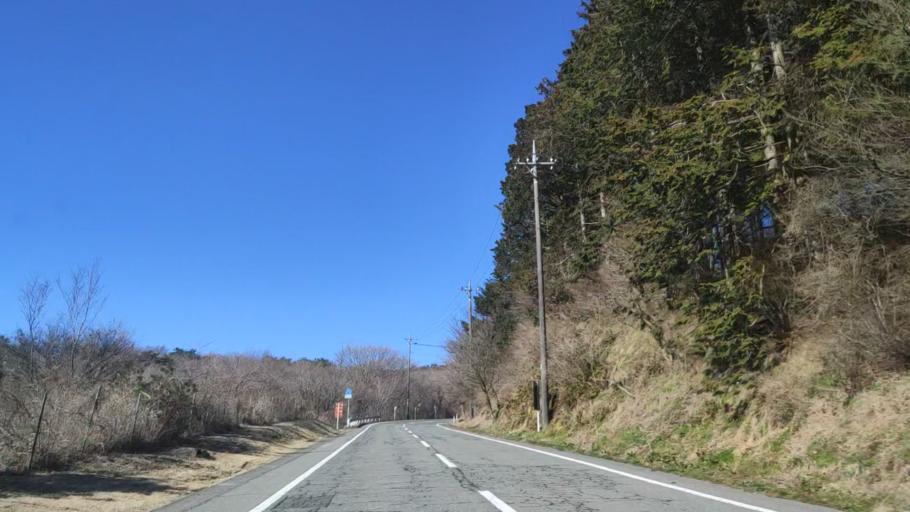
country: JP
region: Yamanashi
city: Fujikawaguchiko
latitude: 35.3844
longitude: 138.6057
